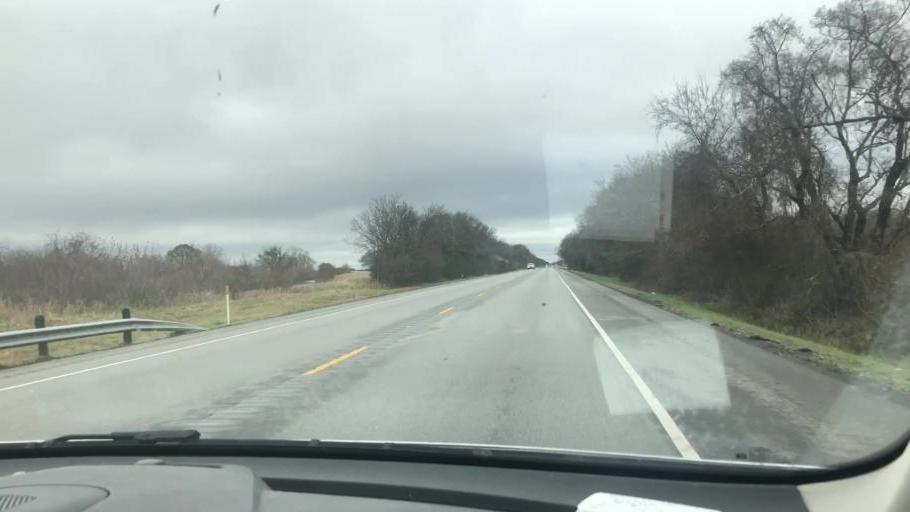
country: US
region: Texas
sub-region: Matagorda County
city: Bay City
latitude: 29.1095
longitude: -95.9789
